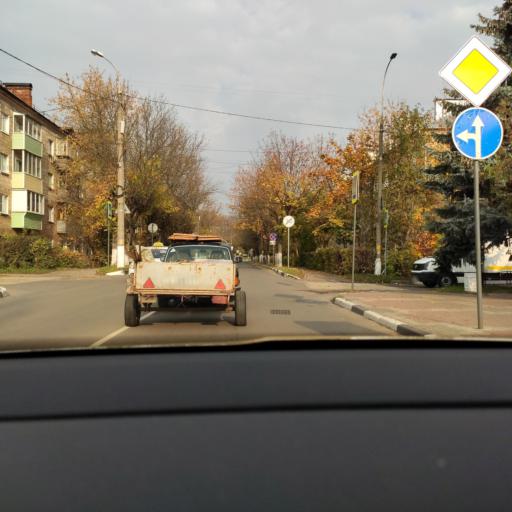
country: RU
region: Moskovskaya
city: Ivanteyevka
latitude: 55.9718
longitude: 37.9050
